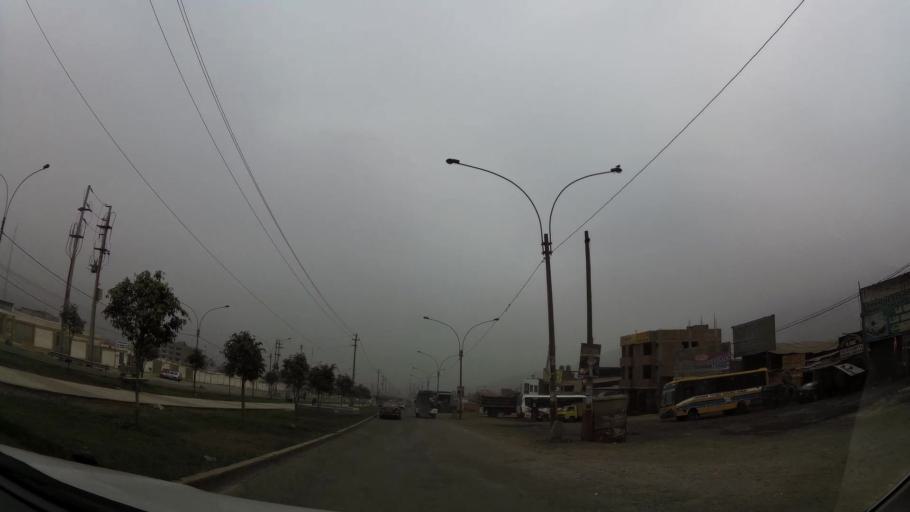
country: PE
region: Lima
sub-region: Lima
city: Urb. Santo Domingo
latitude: -11.9218
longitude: -76.9627
